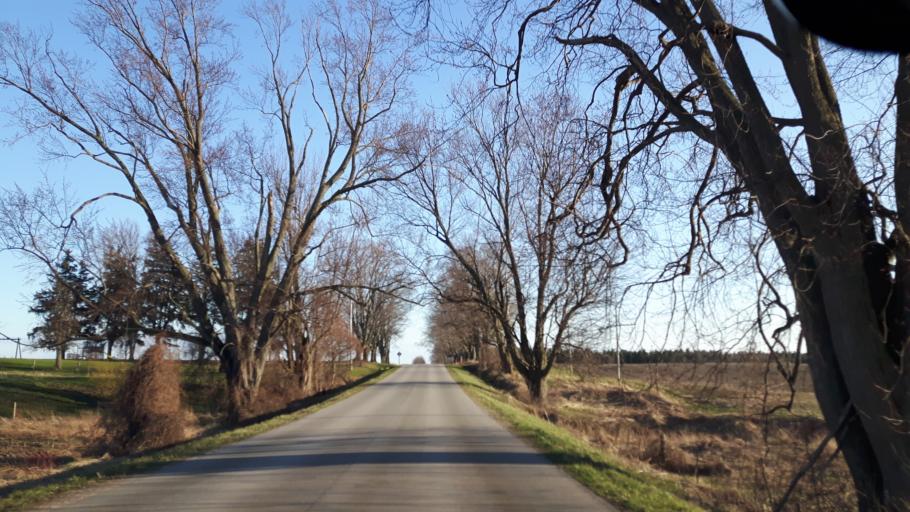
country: CA
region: Ontario
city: Goderich
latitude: 43.6414
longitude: -81.6846
